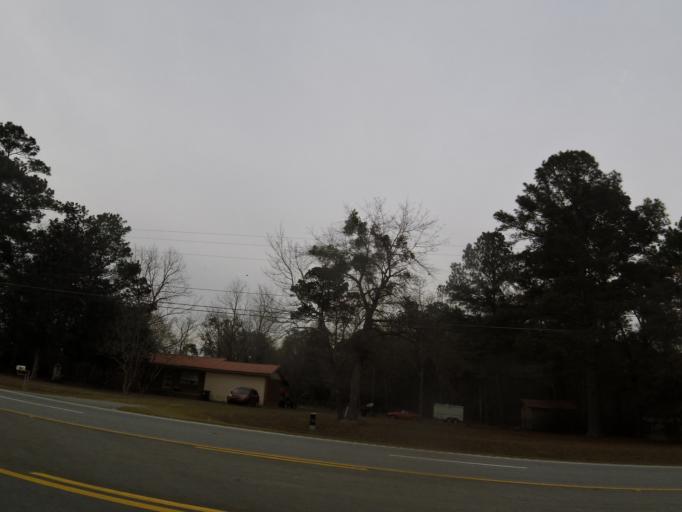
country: US
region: Georgia
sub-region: Grady County
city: Cairo
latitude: 30.8683
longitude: -84.1186
